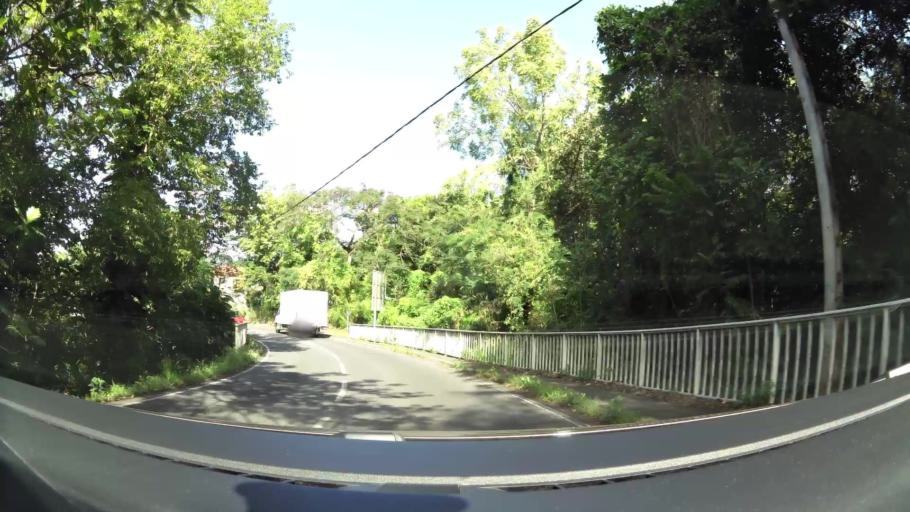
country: GP
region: Guadeloupe
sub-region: Guadeloupe
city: Bouillante
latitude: 16.1458
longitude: -61.7692
